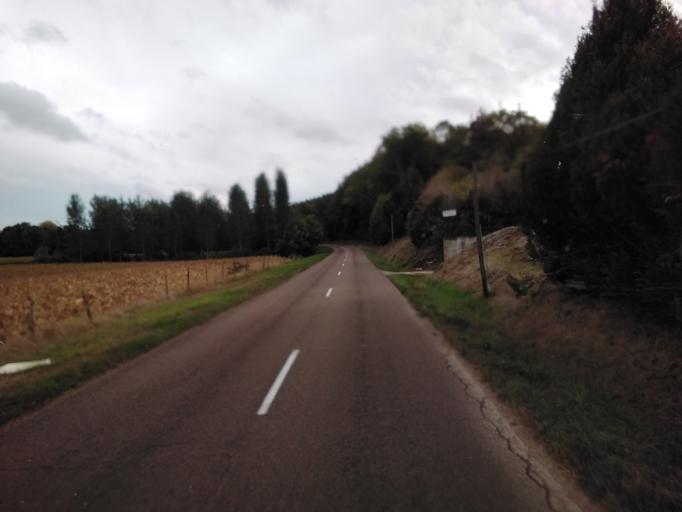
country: FR
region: Champagne-Ardenne
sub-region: Departement de l'Aube
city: Les Riceys
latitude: 47.9741
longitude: 4.3556
